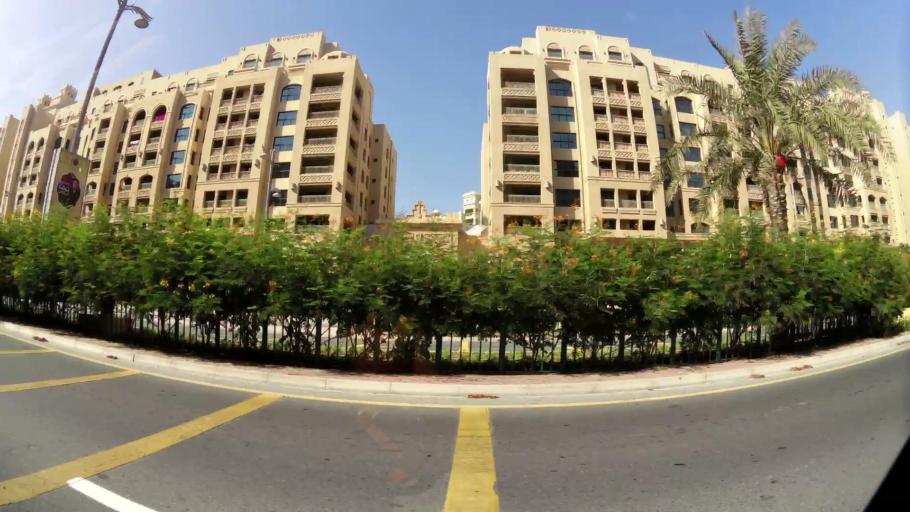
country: AE
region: Dubai
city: Dubai
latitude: 25.1108
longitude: 55.1411
